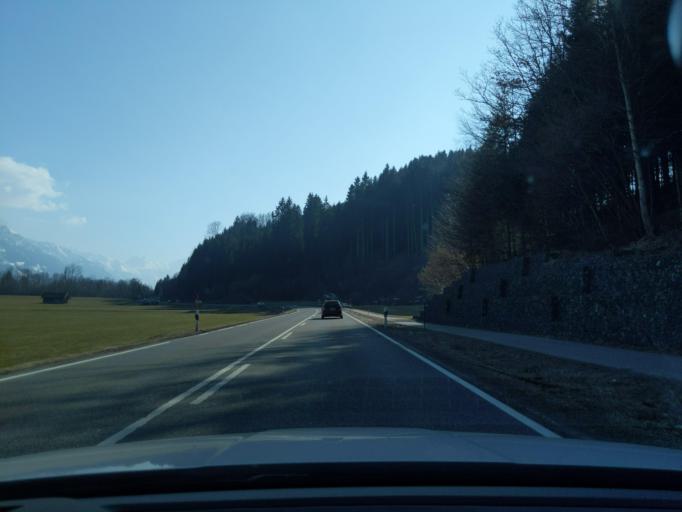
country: DE
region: Bavaria
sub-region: Swabia
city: Sonthofen
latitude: 47.4975
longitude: 10.2656
